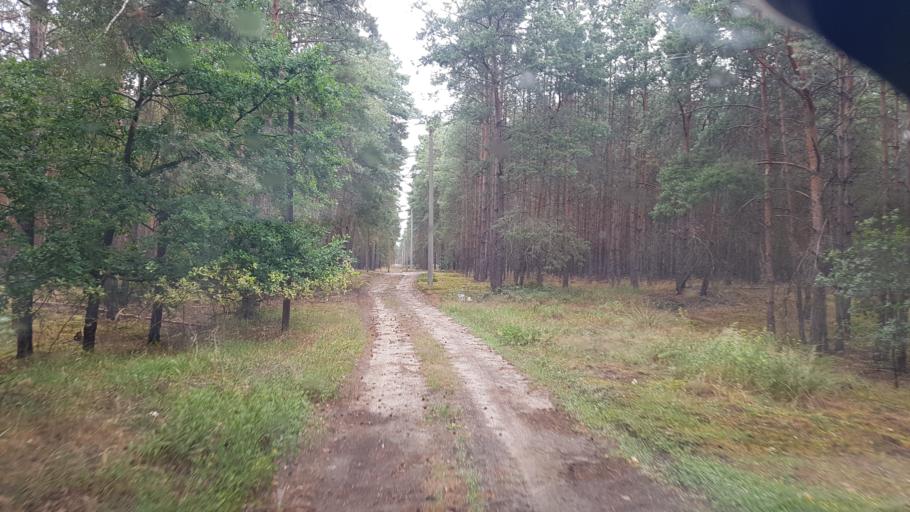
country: DE
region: Brandenburg
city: Schilda
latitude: 51.6365
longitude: 13.3522
